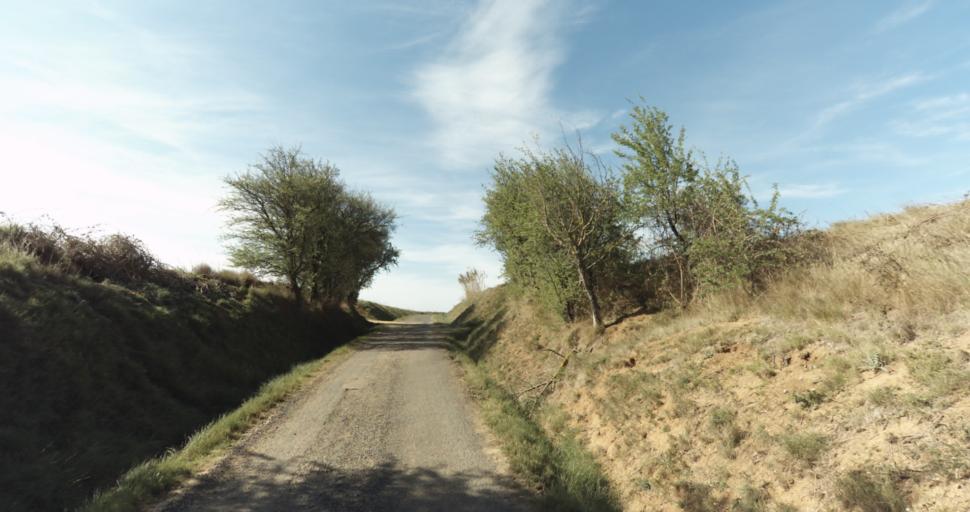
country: FR
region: Languedoc-Roussillon
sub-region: Departement de l'Herault
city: Marseillan
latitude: 43.3476
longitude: 3.5182
